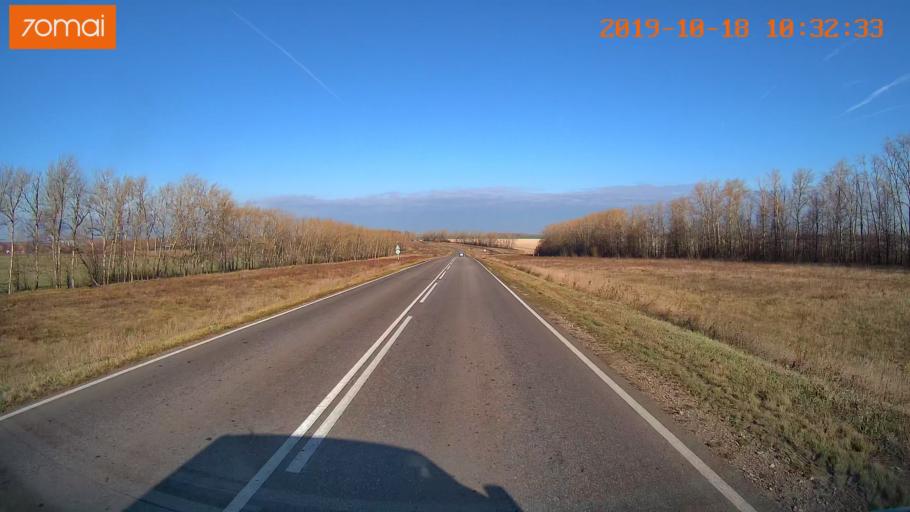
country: RU
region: Tula
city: Kurkino
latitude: 53.4956
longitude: 38.6216
